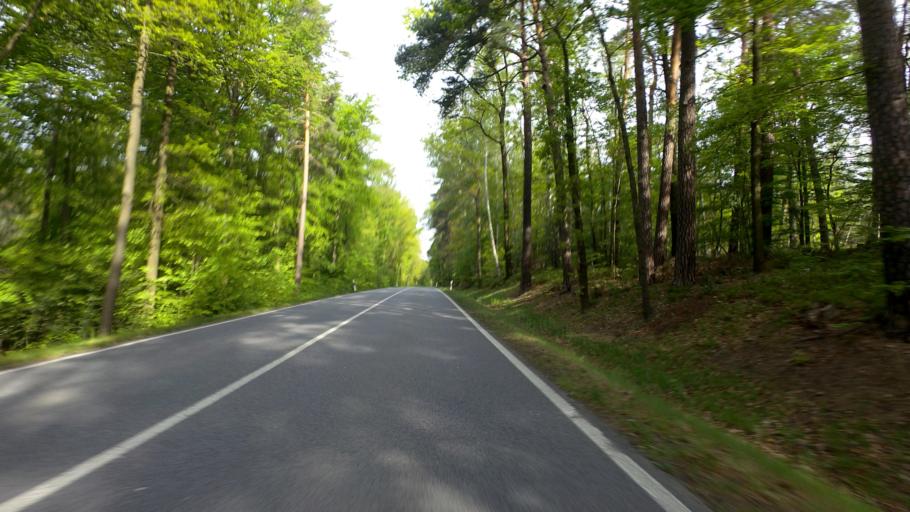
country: DE
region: Saxony
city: Stolpen
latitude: 51.0707
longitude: 14.0437
